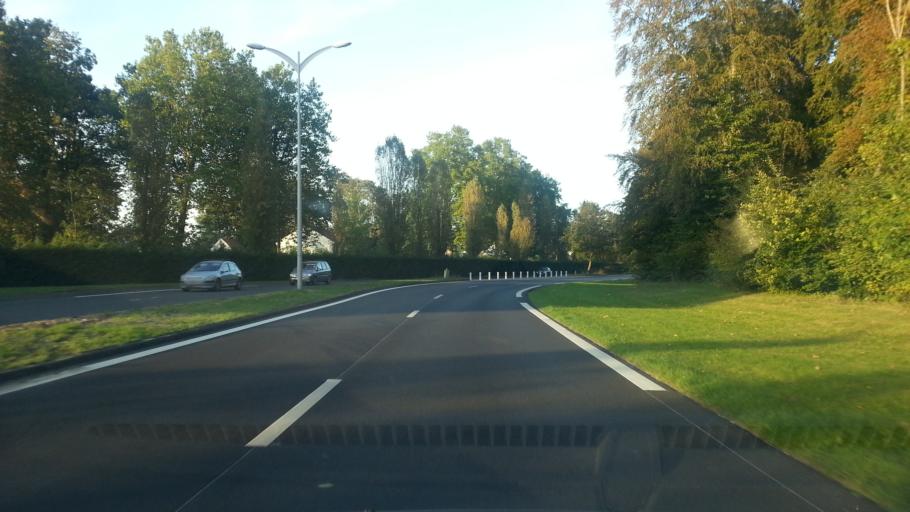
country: FR
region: Picardie
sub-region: Departement de l'Oise
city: Venette
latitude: 49.3941
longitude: 2.8053
